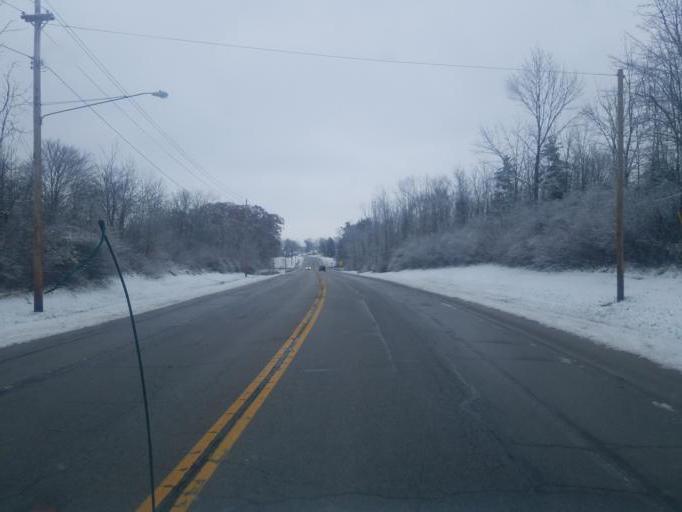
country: US
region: Ohio
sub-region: Geauga County
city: Middlefield
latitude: 41.4657
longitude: -81.0803
